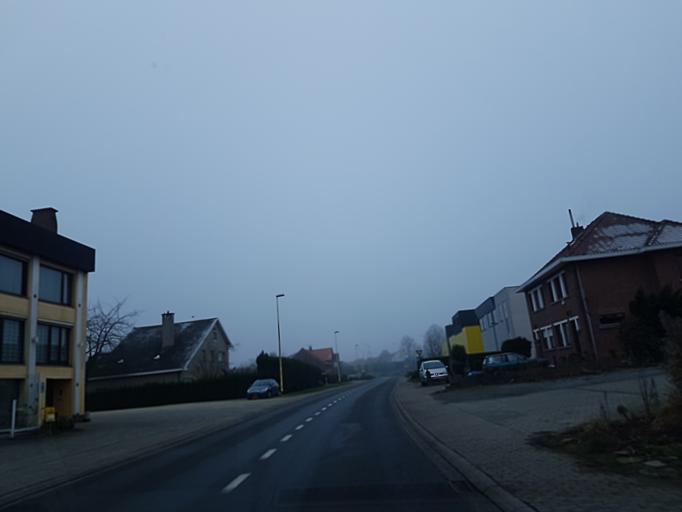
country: BE
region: Flanders
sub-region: Provincie Vlaams-Brabant
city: Meise
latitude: 50.9580
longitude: 4.3175
